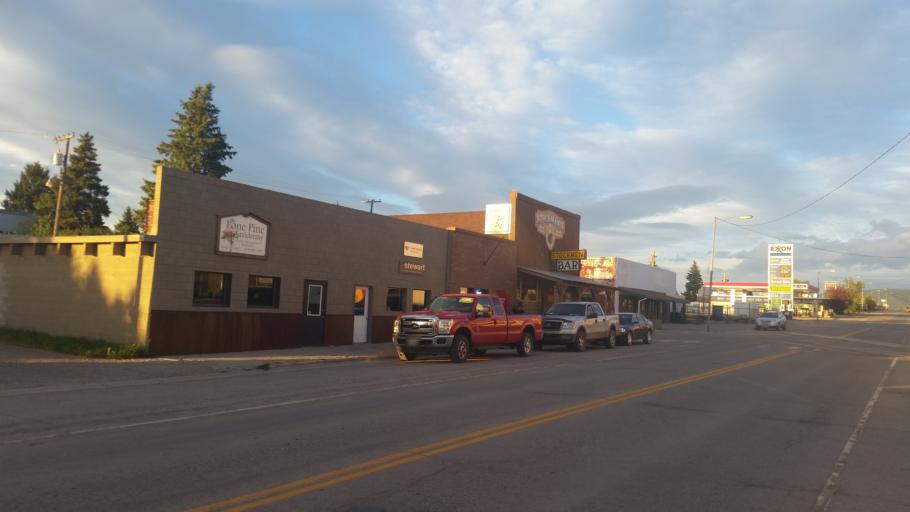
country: US
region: Montana
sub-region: Meagher County
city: White Sulphur Springs
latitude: 46.5482
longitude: -110.9025
